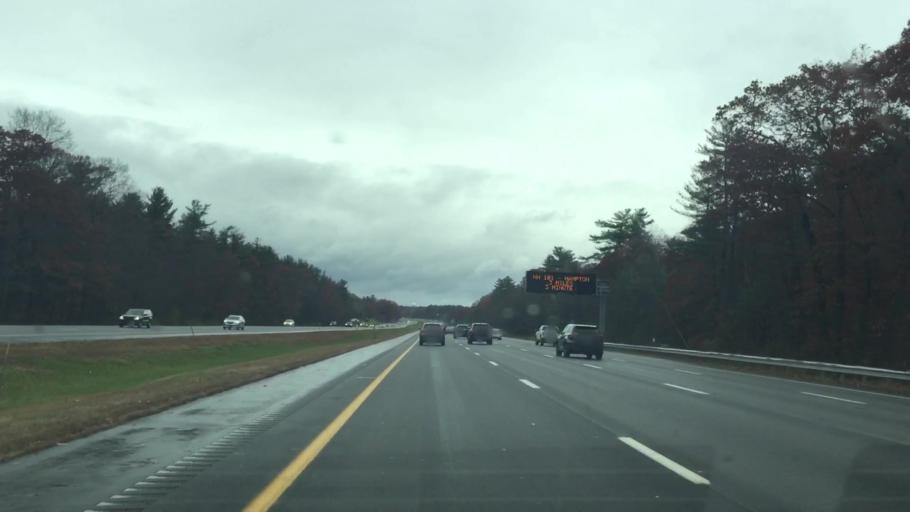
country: US
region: New Hampshire
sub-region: Rockingham County
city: Hampton Falls
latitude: 42.9222
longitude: -70.8686
